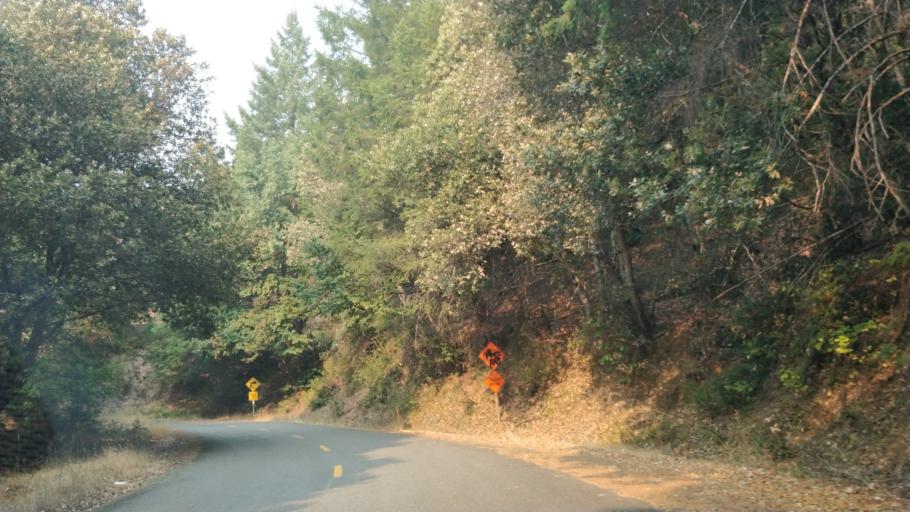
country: US
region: California
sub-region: Humboldt County
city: Rio Dell
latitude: 40.2562
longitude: -124.1202
